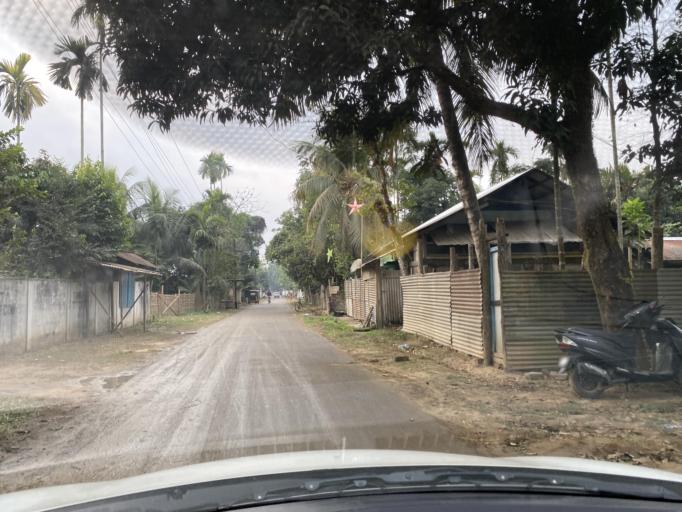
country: IN
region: Assam
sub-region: Cachar
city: Lakhipur
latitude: 24.7874
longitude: 92.9927
